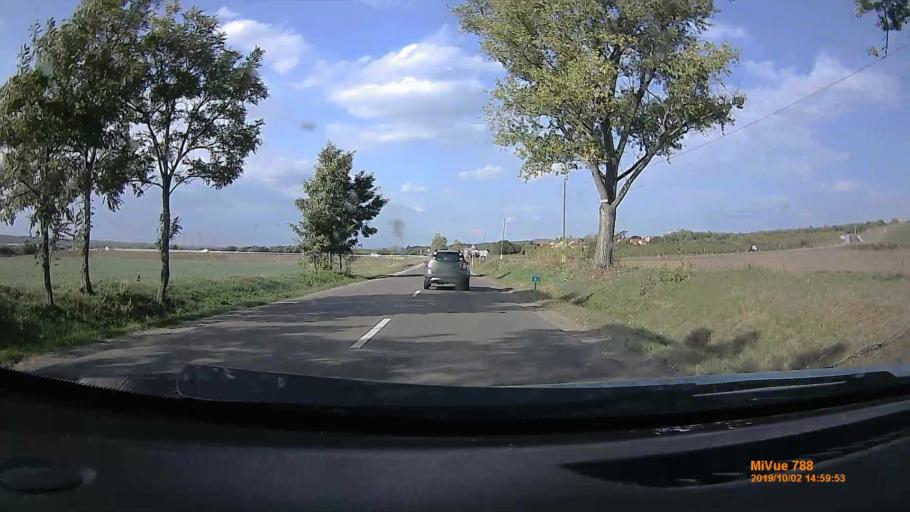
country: HU
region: Heves
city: Andornaktalya
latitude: 47.8290
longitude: 20.4190
